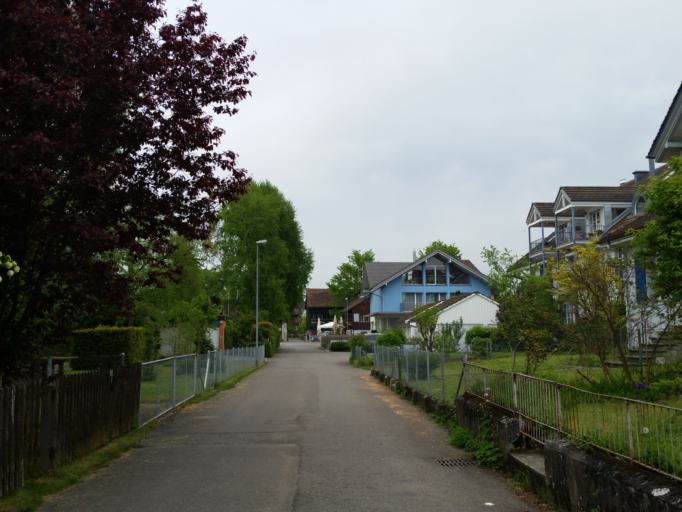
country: CH
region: Thurgau
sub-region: Arbon District
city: Uttwil
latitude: 47.5965
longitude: 9.3212
